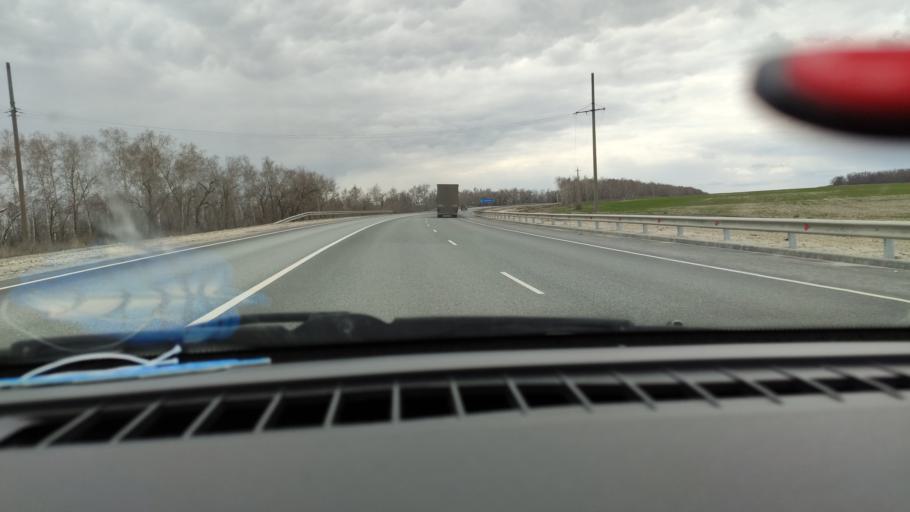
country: RU
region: Saratov
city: Sinodskoye
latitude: 51.9002
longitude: 46.5408
